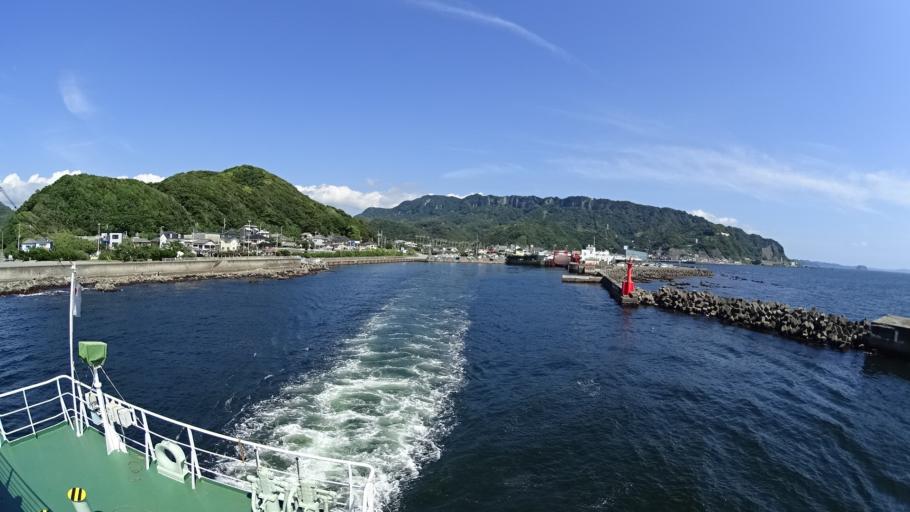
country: JP
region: Chiba
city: Futtsu
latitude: 35.1713
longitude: 139.8154
